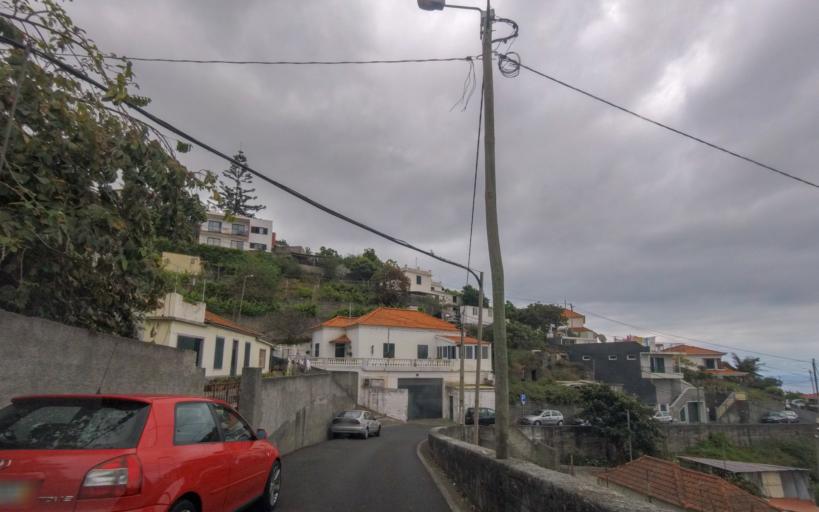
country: PT
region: Madeira
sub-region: Funchal
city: Nossa Senhora do Monte
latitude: 32.6616
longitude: -16.8882
